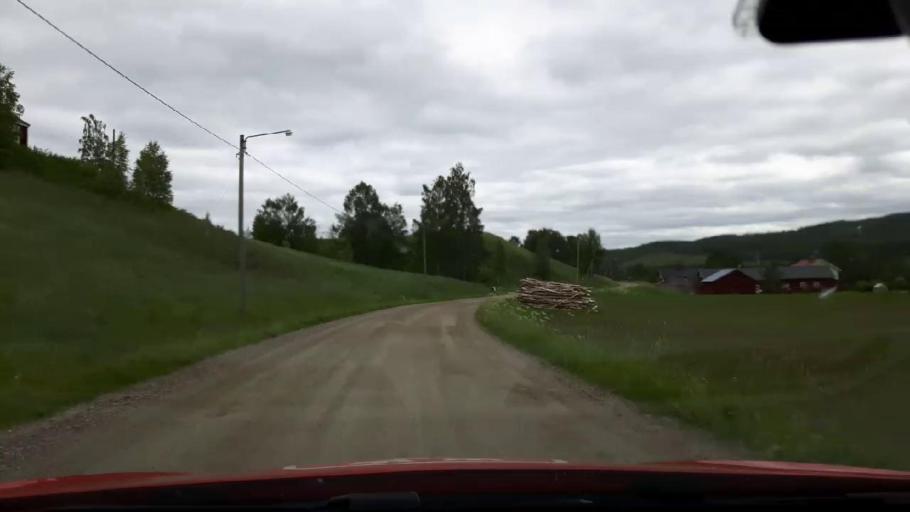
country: SE
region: Jaemtland
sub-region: Ragunda Kommun
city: Hammarstrand
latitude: 63.1642
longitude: 16.2176
